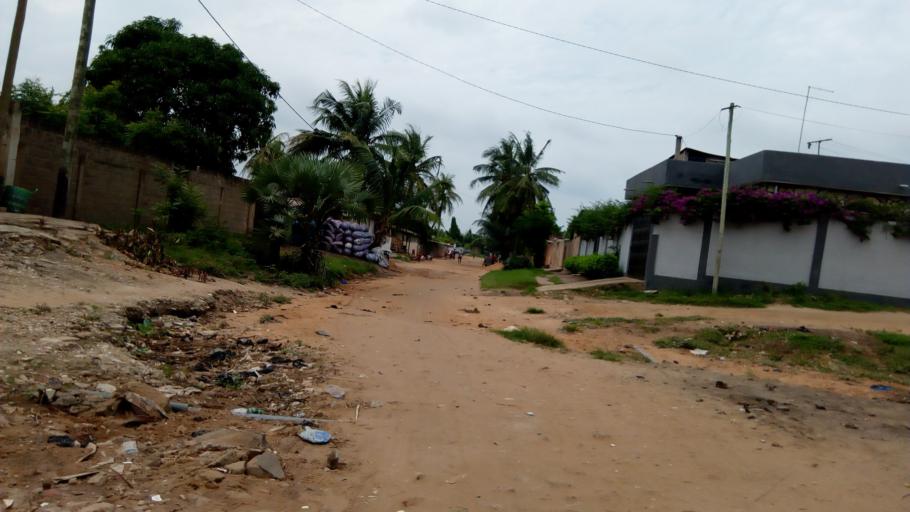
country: TG
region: Maritime
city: Lome
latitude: 6.1674
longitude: 1.2069
